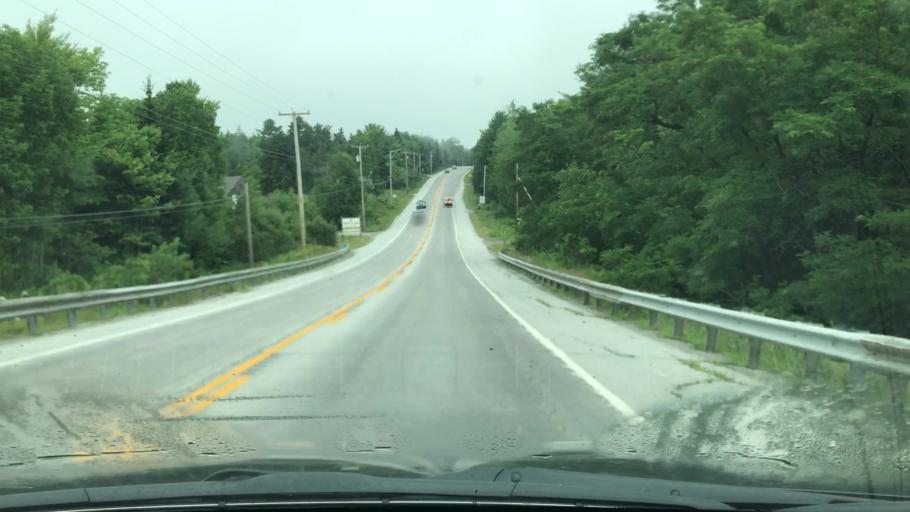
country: US
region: Maine
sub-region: Waldo County
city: Northport
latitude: 44.3052
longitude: -68.9769
